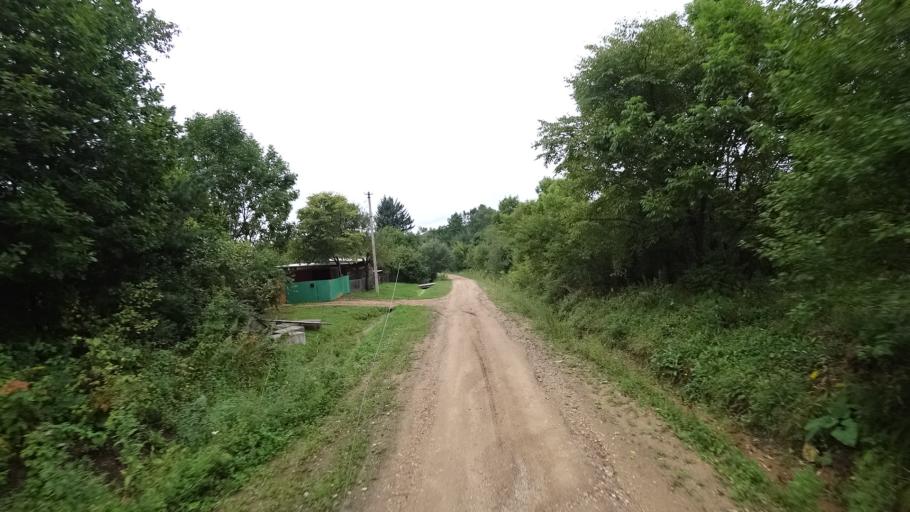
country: RU
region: Primorskiy
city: Rettikhovka
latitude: 44.1610
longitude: 132.7432
